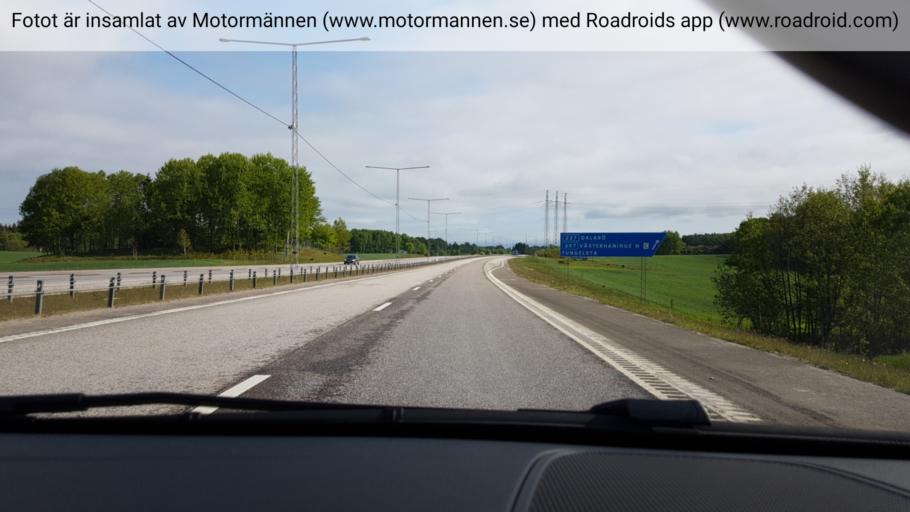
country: SE
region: Stockholm
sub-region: Haninge Kommun
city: Jordbro
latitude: 59.1166
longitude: 18.1285
